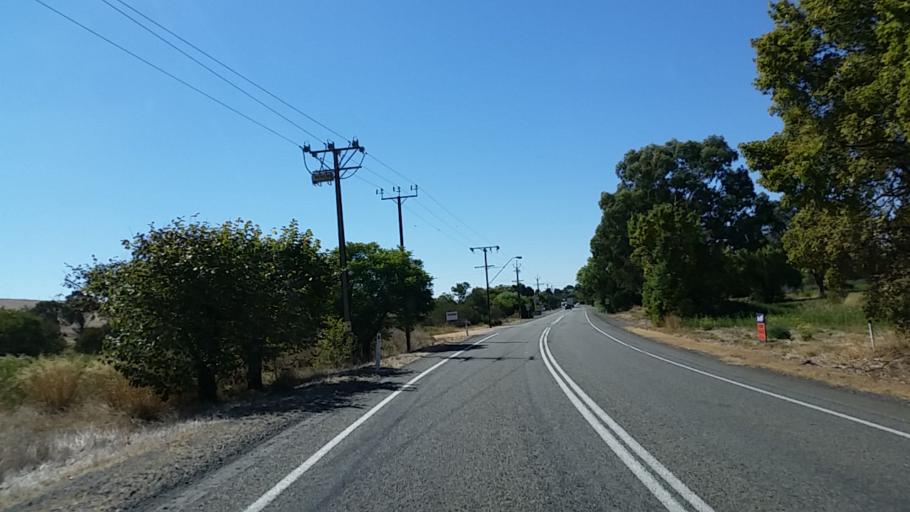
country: AU
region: South Australia
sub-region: Light
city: Kapunda
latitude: -34.0881
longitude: 138.7760
